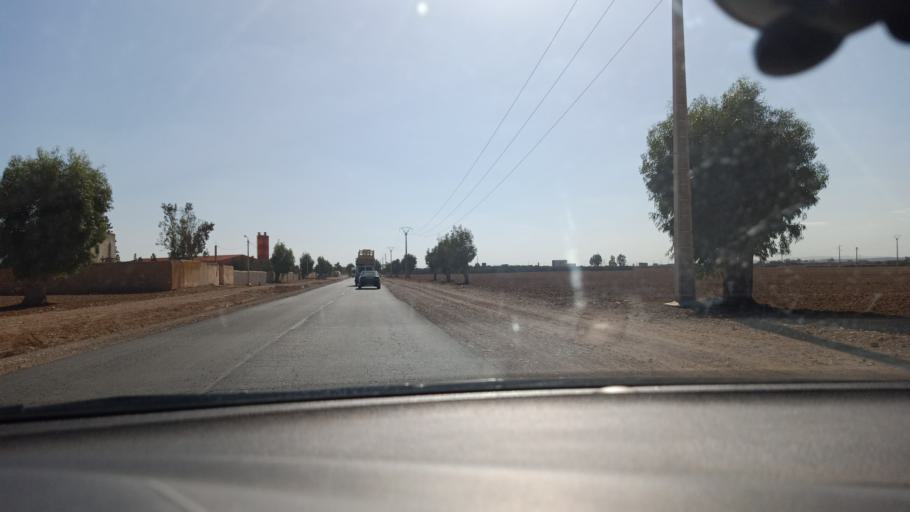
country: MA
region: Doukkala-Abda
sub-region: Safi
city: Youssoufia
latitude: 32.1041
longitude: -8.6111
